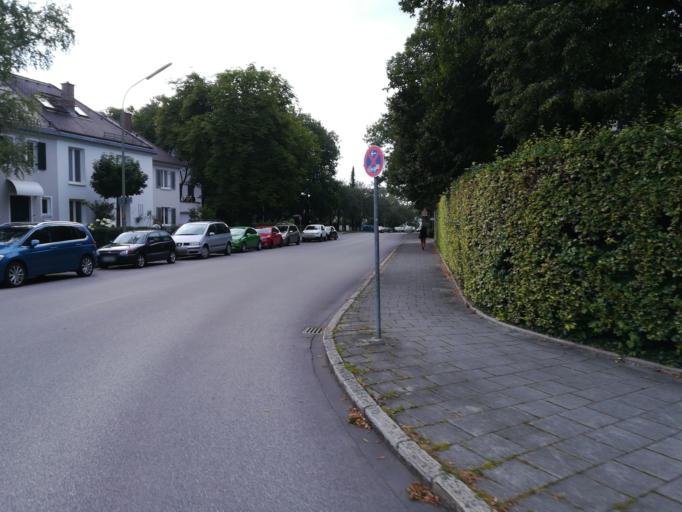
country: DE
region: Bavaria
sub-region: Upper Bavaria
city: Munich
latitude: 48.1626
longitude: 11.5215
